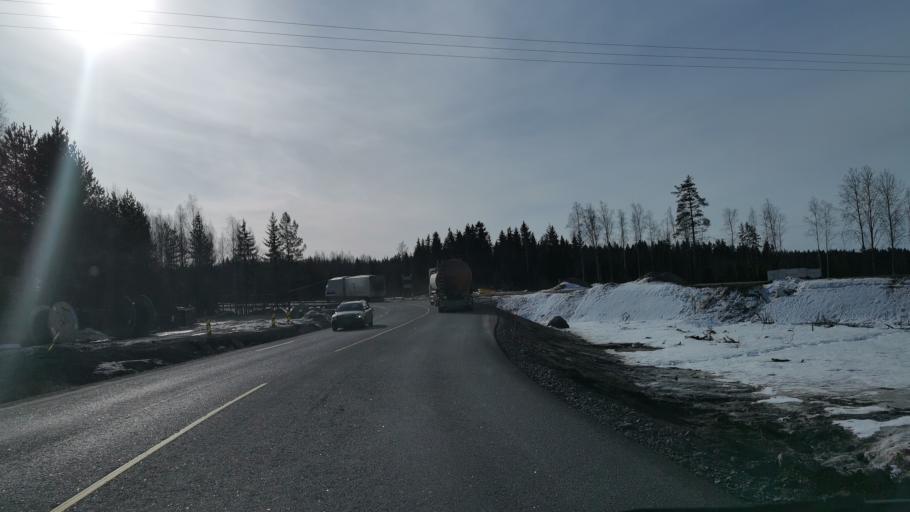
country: FI
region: Kymenlaakso
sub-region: Kouvola
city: Kouvola
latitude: 60.8686
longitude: 26.5513
